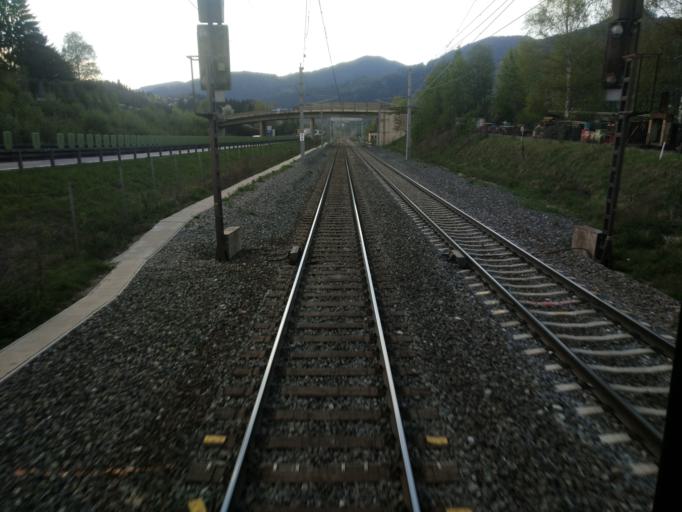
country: AT
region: Styria
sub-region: Politischer Bezirk Bruck-Muerzzuschlag
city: Oberaich
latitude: 47.4048
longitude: 15.2181
